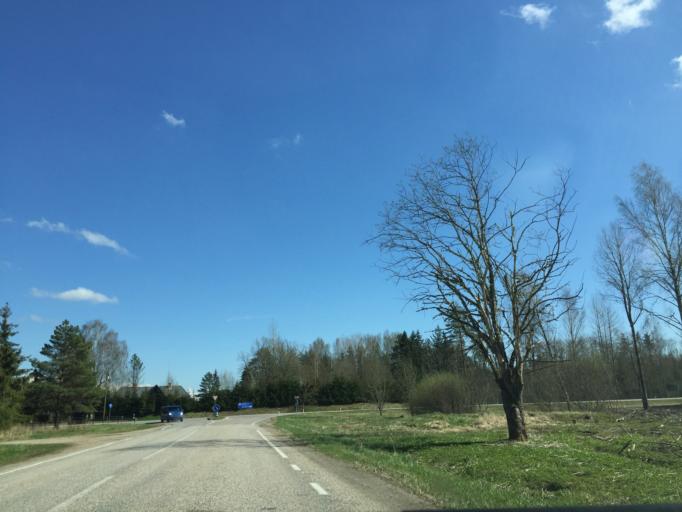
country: EE
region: Valgamaa
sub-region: Valga linn
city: Valga
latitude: 57.8498
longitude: 26.1302
